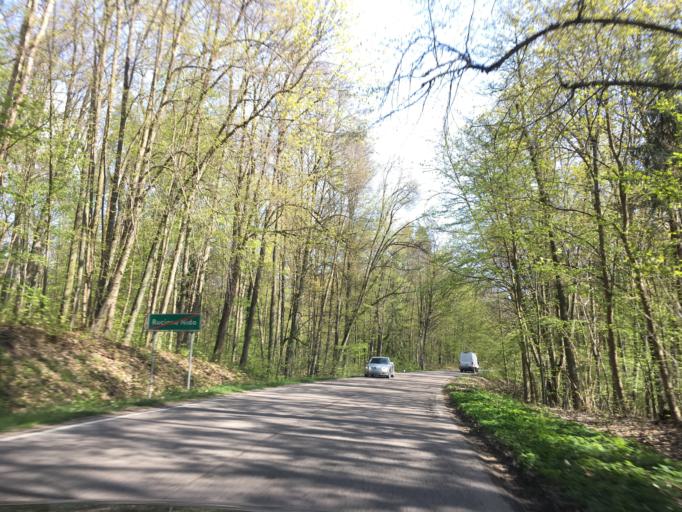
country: PL
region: Warmian-Masurian Voivodeship
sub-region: Powiat piski
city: Ruciane-Nida
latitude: 53.6639
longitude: 21.5682
